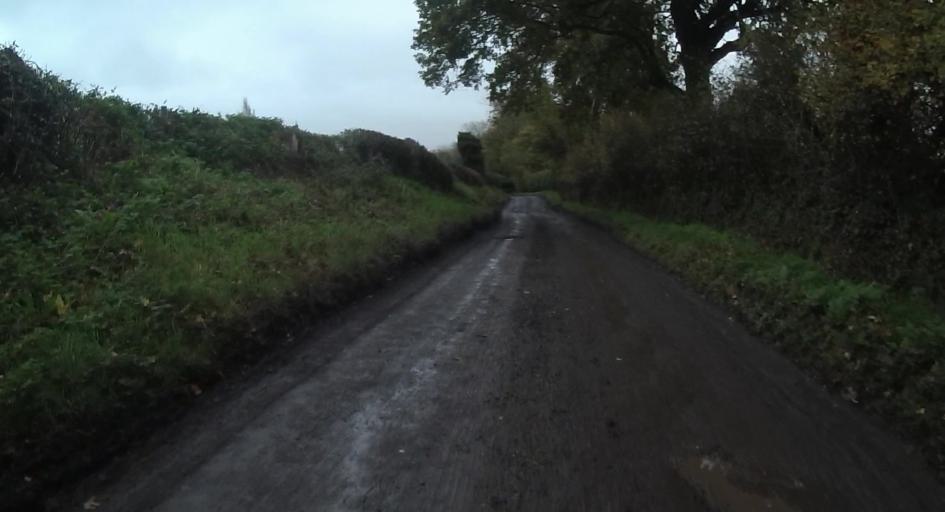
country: GB
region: England
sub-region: Surrey
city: Farnham
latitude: 51.2215
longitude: -0.8084
